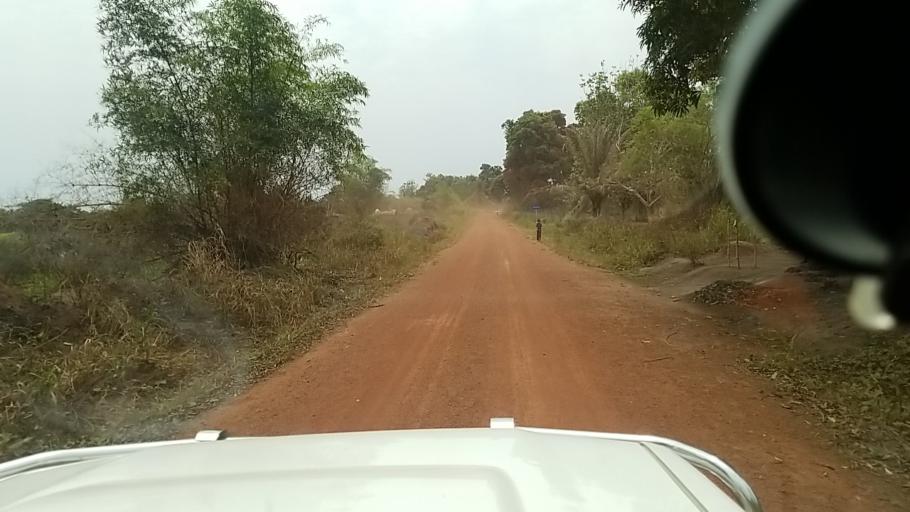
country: CD
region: Equateur
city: Libenge
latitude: 3.7346
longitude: 18.7772
